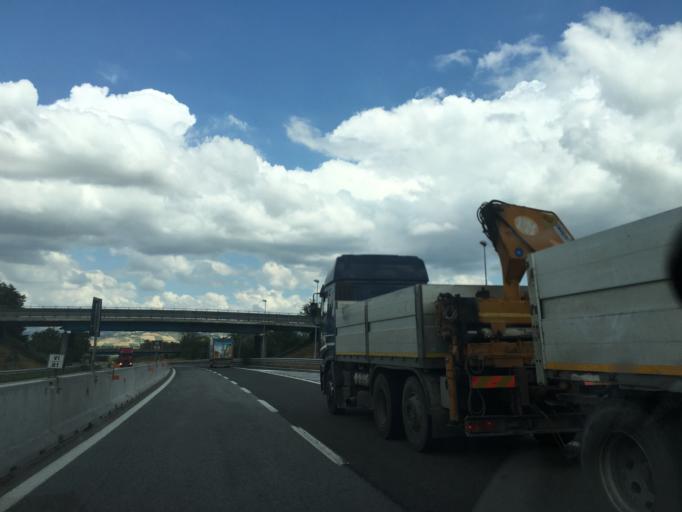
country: IT
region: Campania
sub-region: Provincia di Avellino
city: Grottaminarda
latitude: 41.0639
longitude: 15.0622
